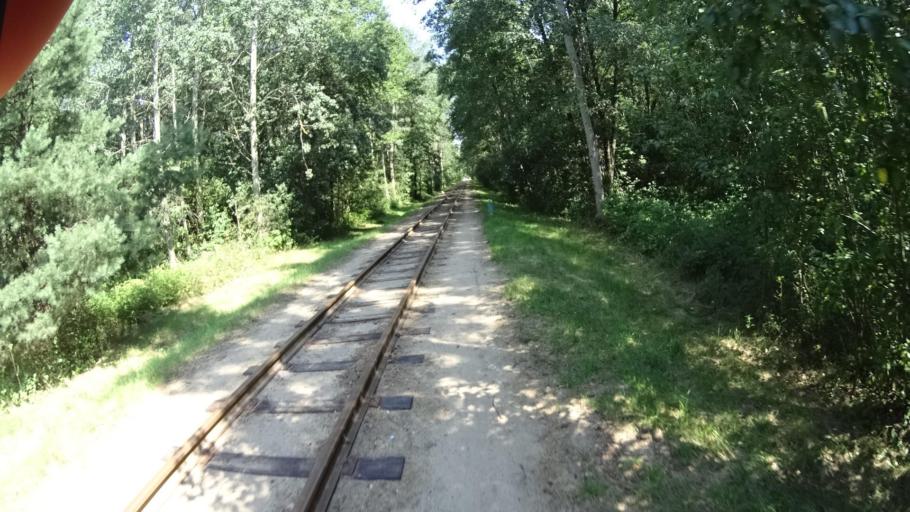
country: PL
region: Masovian Voivodeship
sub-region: Powiat piaseczynski
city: Tarczyn
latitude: 51.9883
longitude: 20.8852
